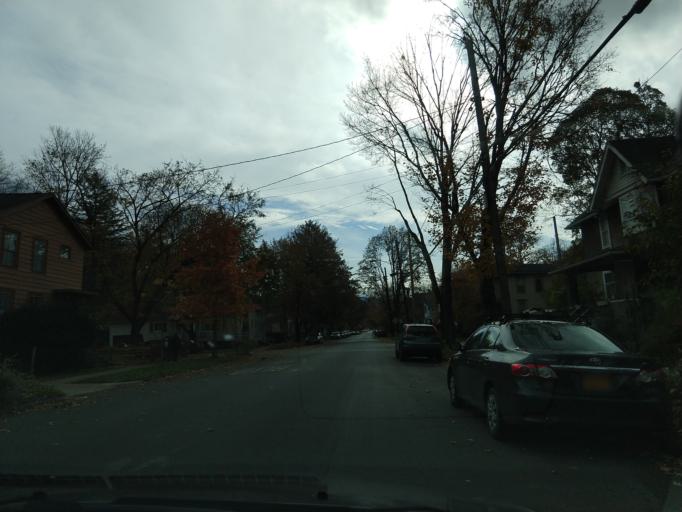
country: US
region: New York
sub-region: Tompkins County
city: Ithaca
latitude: 42.4477
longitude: -76.4973
